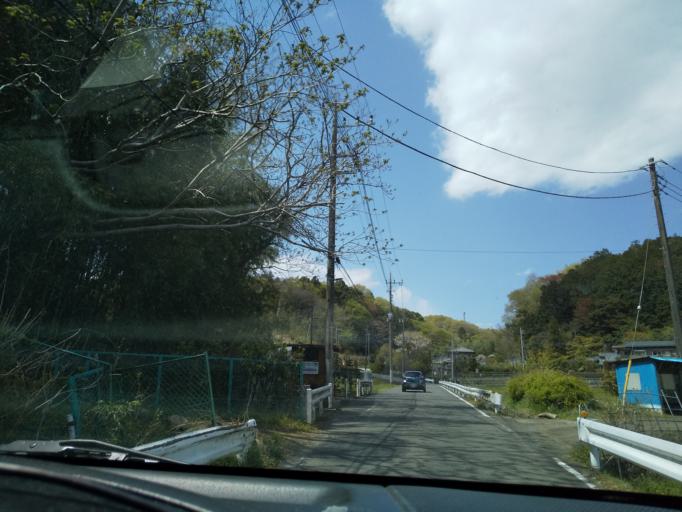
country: JP
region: Tokyo
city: Hino
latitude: 35.6019
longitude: 139.3958
